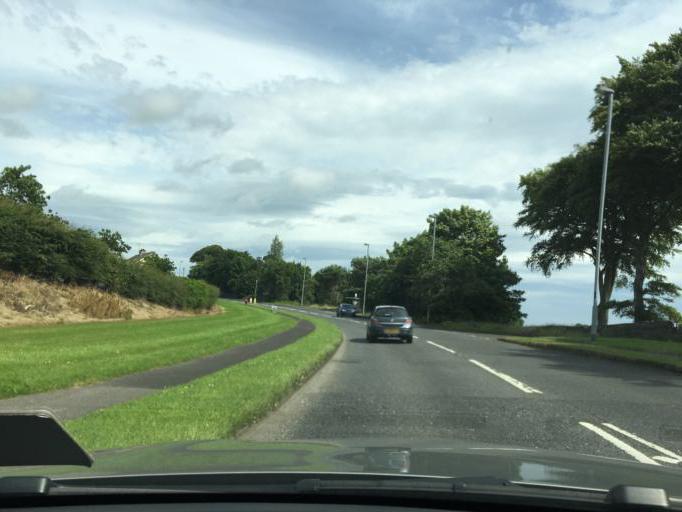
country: GB
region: Northern Ireland
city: Culmore
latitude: 55.0380
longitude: -7.2784
